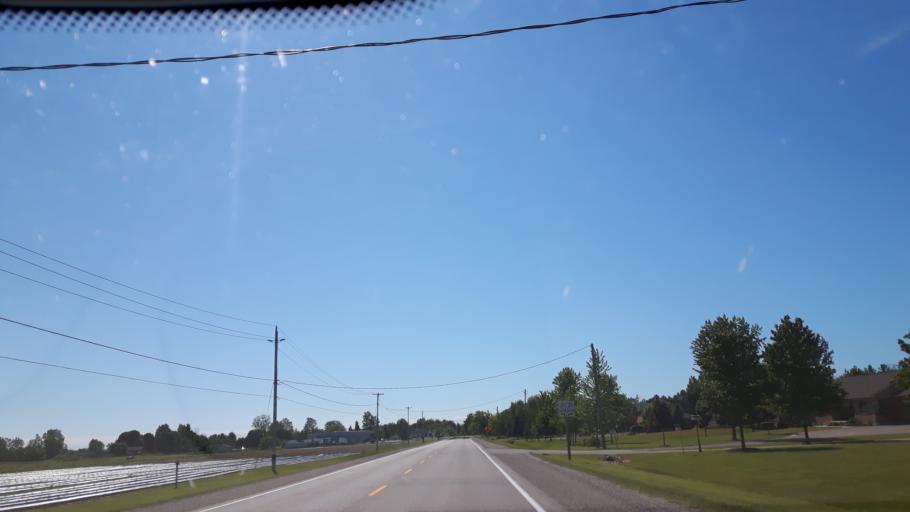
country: CA
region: Ontario
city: Bluewater
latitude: 43.4128
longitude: -81.6998
